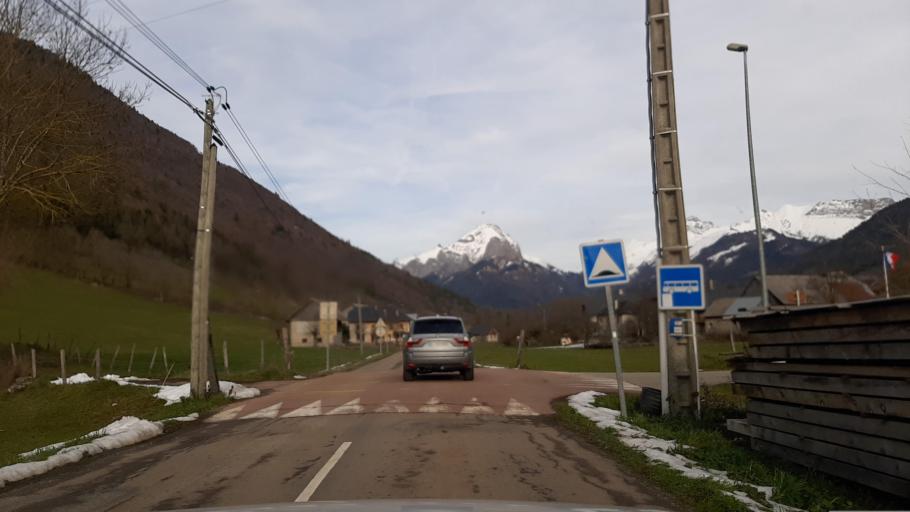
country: FR
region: Rhone-Alpes
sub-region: Departement de la Savoie
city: Coise-Saint-Jean-Pied-Gauthier
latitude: 45.6174
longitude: 6.1440
